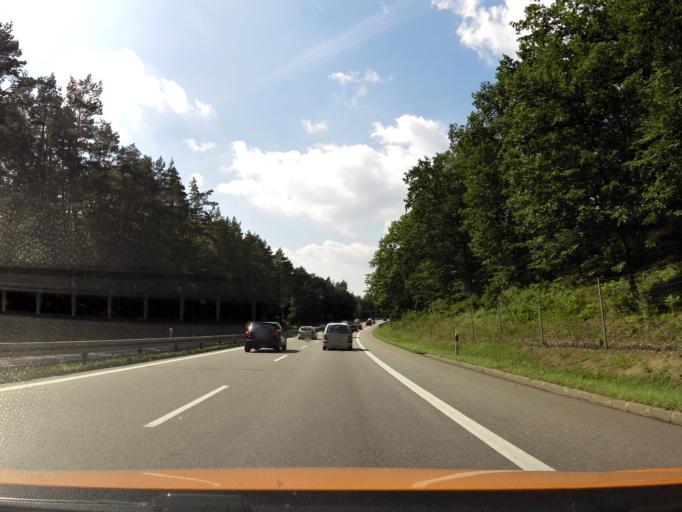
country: PL
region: West Pomeranian Voivodeship
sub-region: Szczecin
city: Szczecin
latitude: 53.3458
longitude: 14.5954
